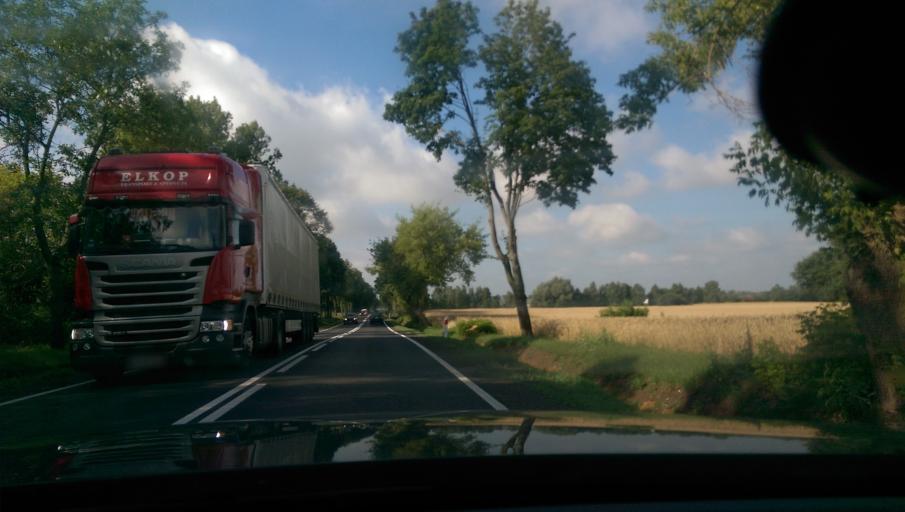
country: PL
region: Masovian Voivodeship
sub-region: Powiat ciechanowski
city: Ojrzen
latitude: 52.7430
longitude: 20.5254
